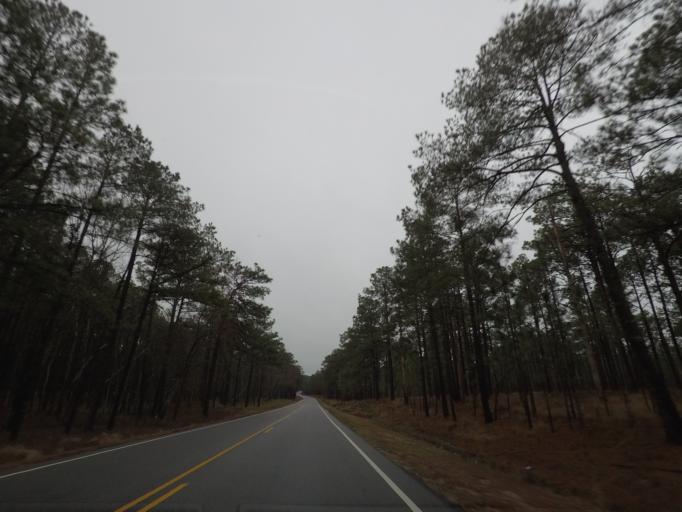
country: US
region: North Carolina
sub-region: Cumberland County
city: Spring Lake
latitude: 35.2431
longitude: -79.0071
